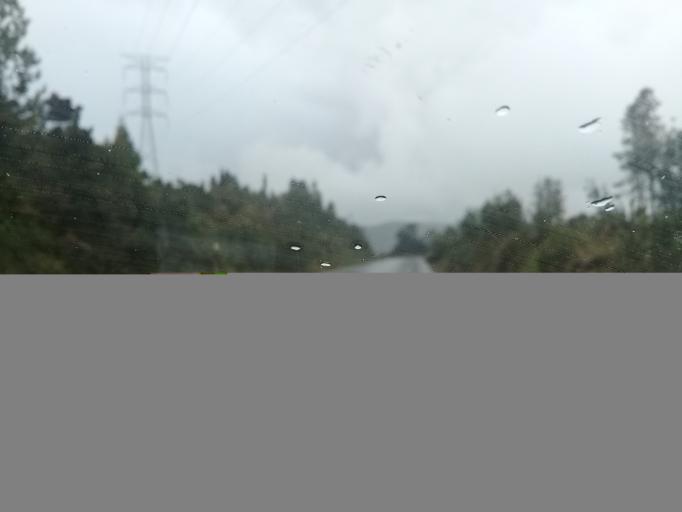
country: CO
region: Cundinamarca
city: Guatavita
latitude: 4.8526
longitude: -73.7772
